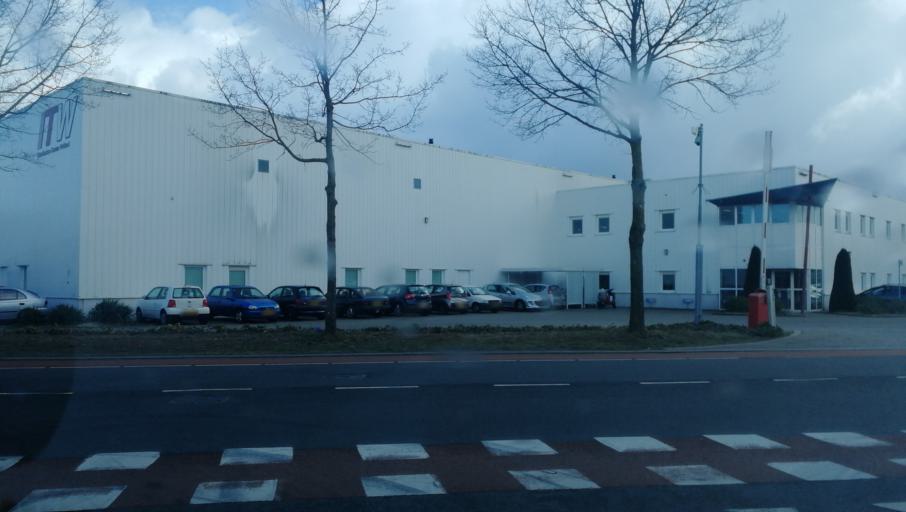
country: NL
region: Limburg
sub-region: Gemeente Peel en Maas
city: Maasbree
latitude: 51.3919
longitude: 6.0880
